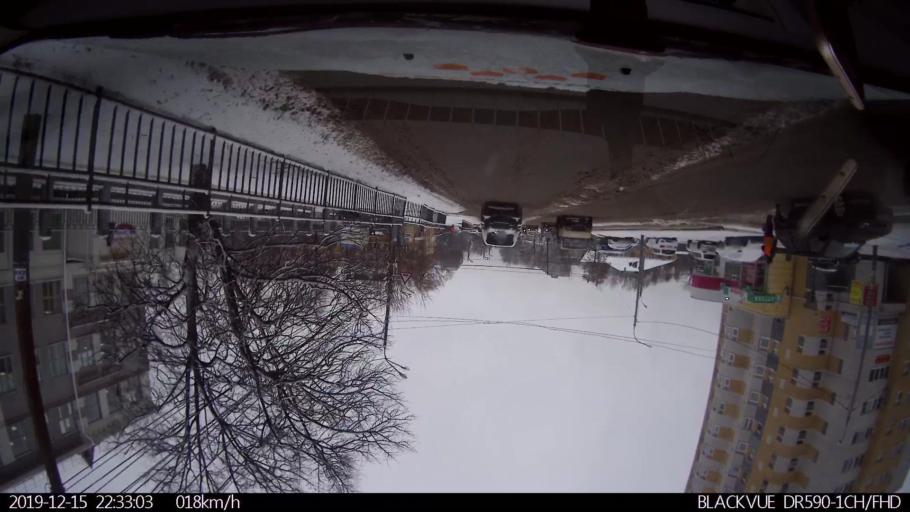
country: RU
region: Nizjnij Novgorod
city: Gorbatovka
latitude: 56.3438
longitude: 43.8376
